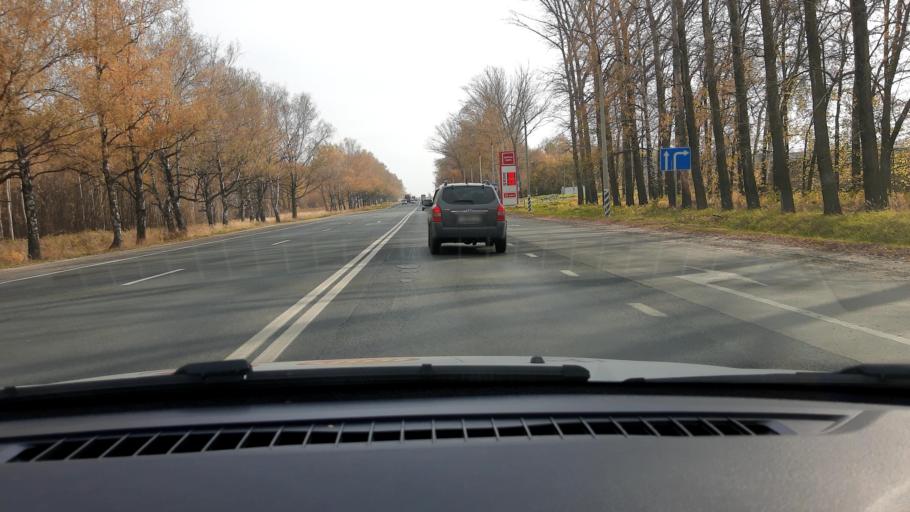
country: RU
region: Nizjnij Novgorod
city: Kstovo
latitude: 56.1374
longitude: 44.2366
